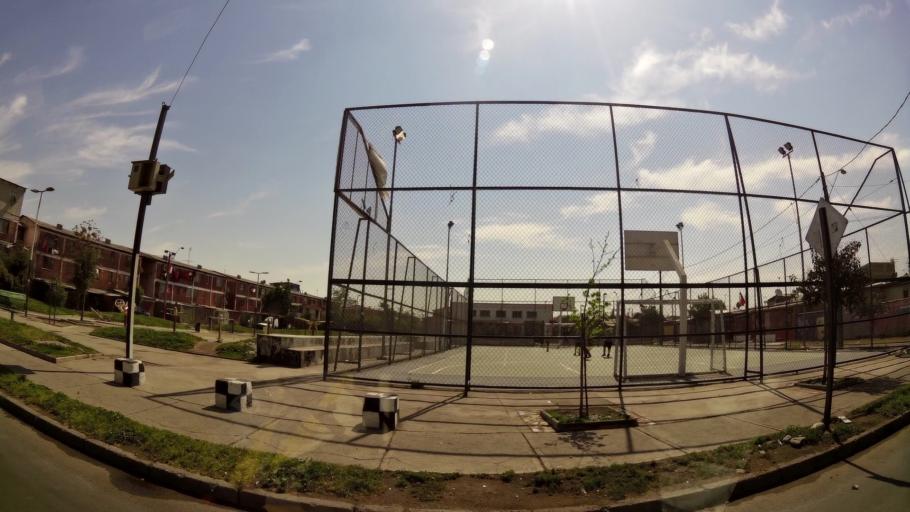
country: CL
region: Santiago Metropolitan
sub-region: Provincia de Santiago
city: La Pintana
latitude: -33.5600
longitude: -70.6335
